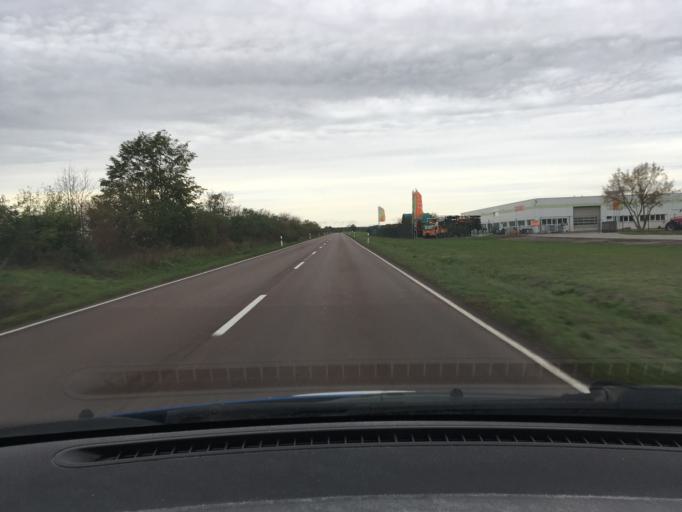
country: DE
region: Saxony-Anhalt
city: Leitzkau
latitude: 52.0201
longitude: 12.0072
